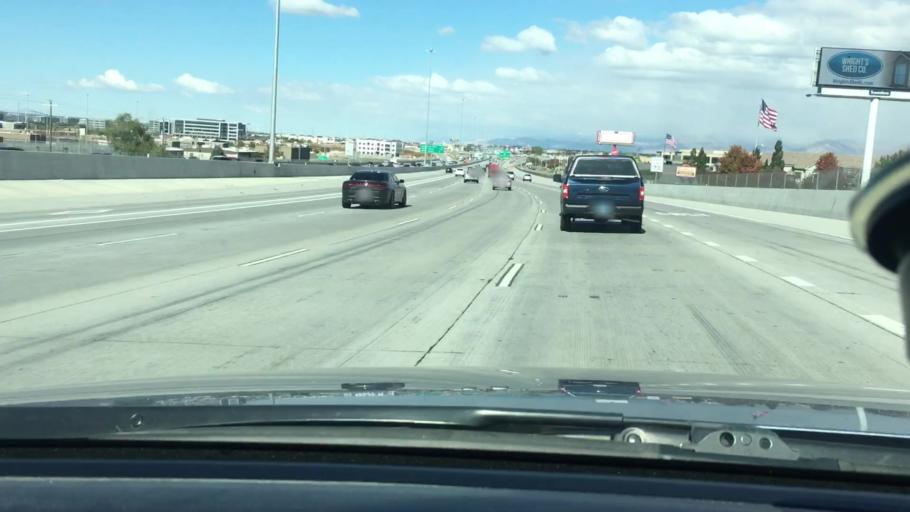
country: US
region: Utah
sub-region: Salt Lake County
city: Draper
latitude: 40.4931
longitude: -111.8908
